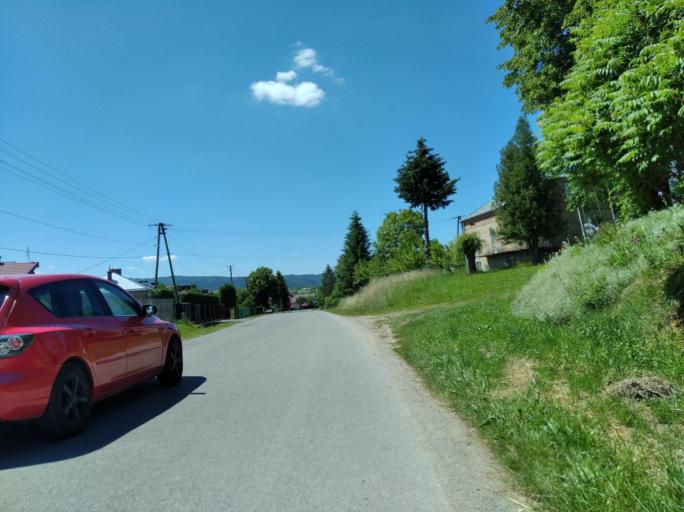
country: PL
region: Subcarpathian Voivodeship
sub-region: Powiat jasielski
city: Nowy Zmigrod
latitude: 49.6205
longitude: 21.5829
